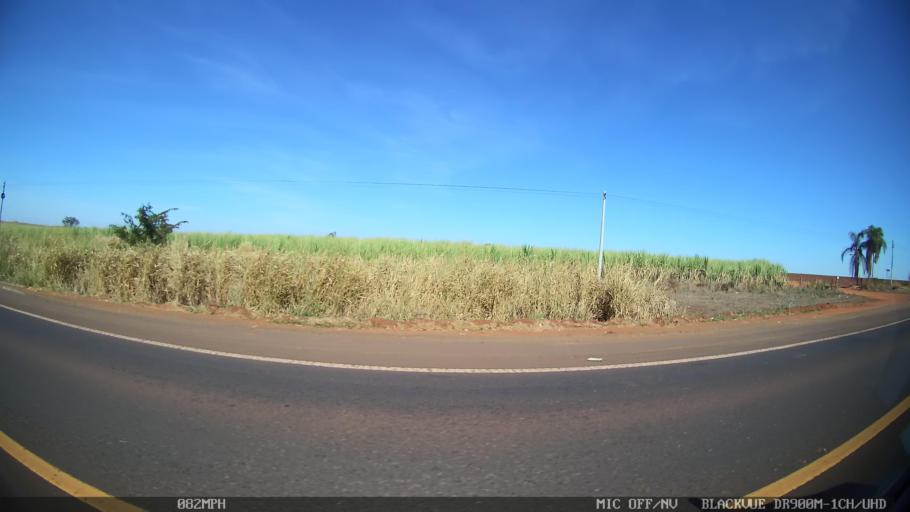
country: BR
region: Sao Paulo
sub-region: Barretos
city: Barretos
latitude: -20.5535
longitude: -48.6387
